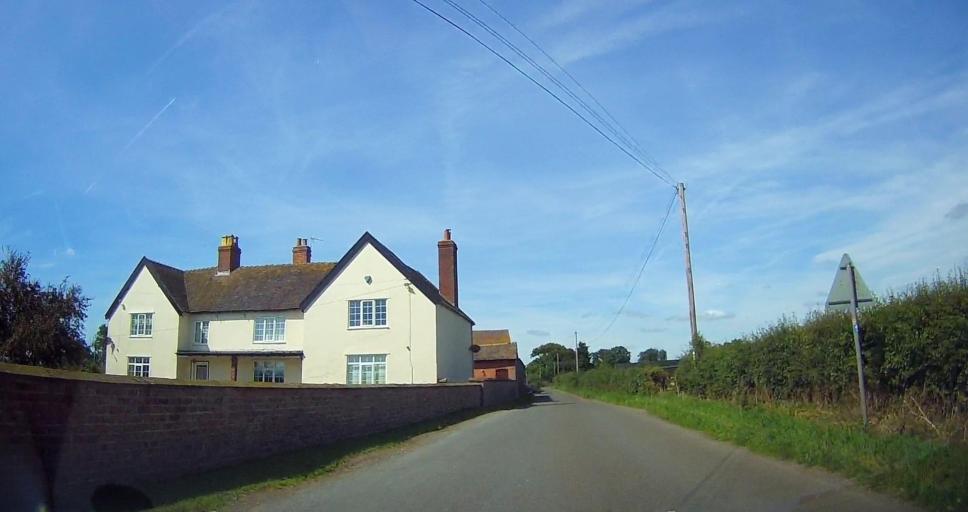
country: GB
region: England
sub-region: Cheshire East
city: Nantwich
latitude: 52.9879
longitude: -2.5332
